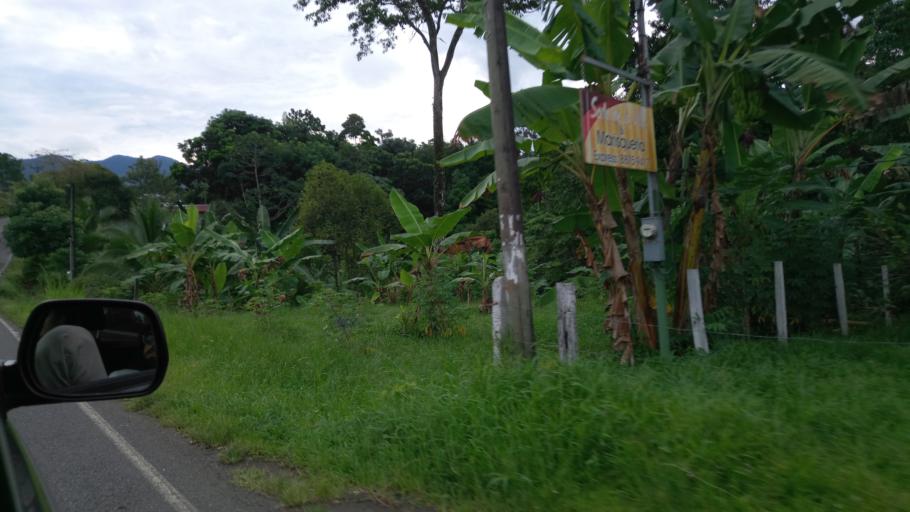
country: CR
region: Alajuela
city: Pocosol
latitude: 10.3636
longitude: -84.5877
